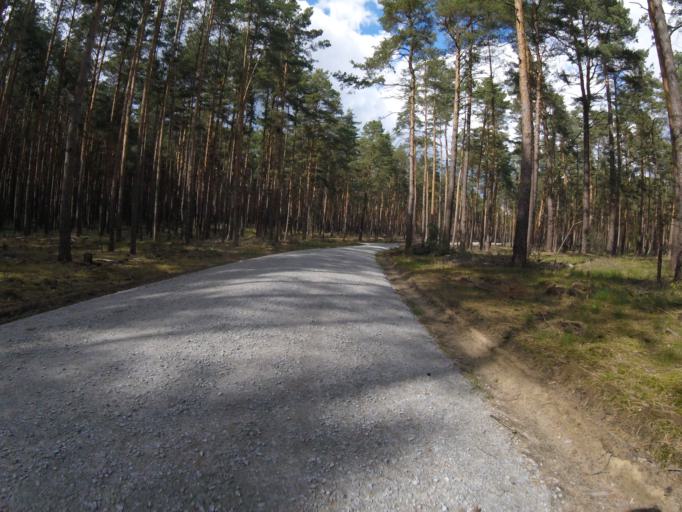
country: DE
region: Brandenburg
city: Schwerin
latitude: 52.1933
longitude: 13.5947
